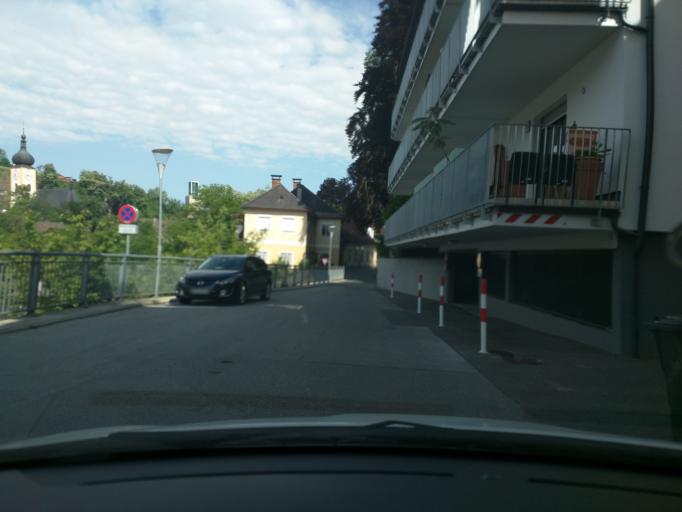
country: AT
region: Lower Austria
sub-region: Waidhofen an der Ybbs Stadt
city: Waidhofen an der Ybbs
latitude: 47.9615
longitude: 14.7771
